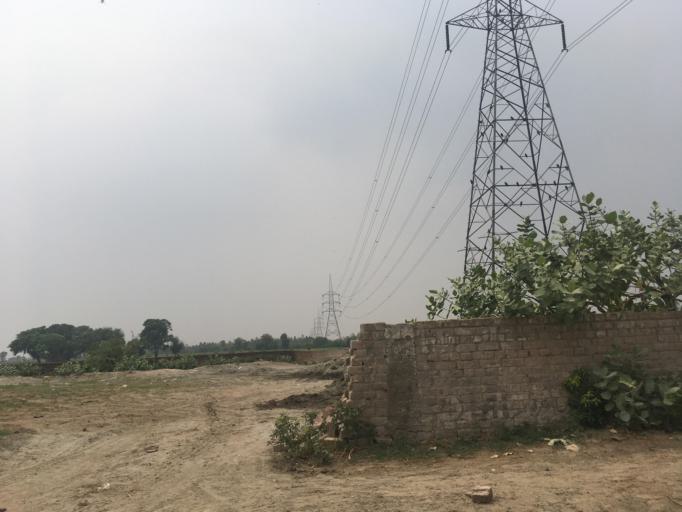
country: PK
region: Punjab
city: Lahore
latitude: 31.6252
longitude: 74.3478
